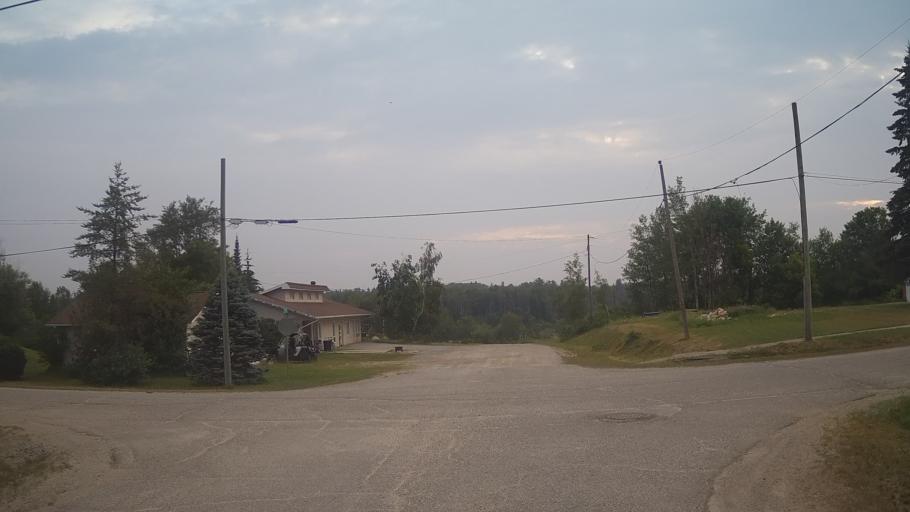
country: CA
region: Ontario
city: Hearst
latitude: 49.6125
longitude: -83.2595
